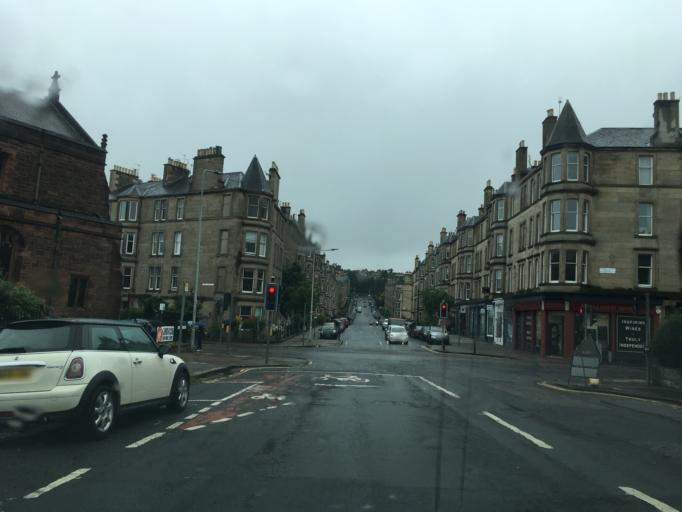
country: GB
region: Scotland
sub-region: Edinburgh
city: Edinburgh
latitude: 55.9599
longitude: -3.2188
